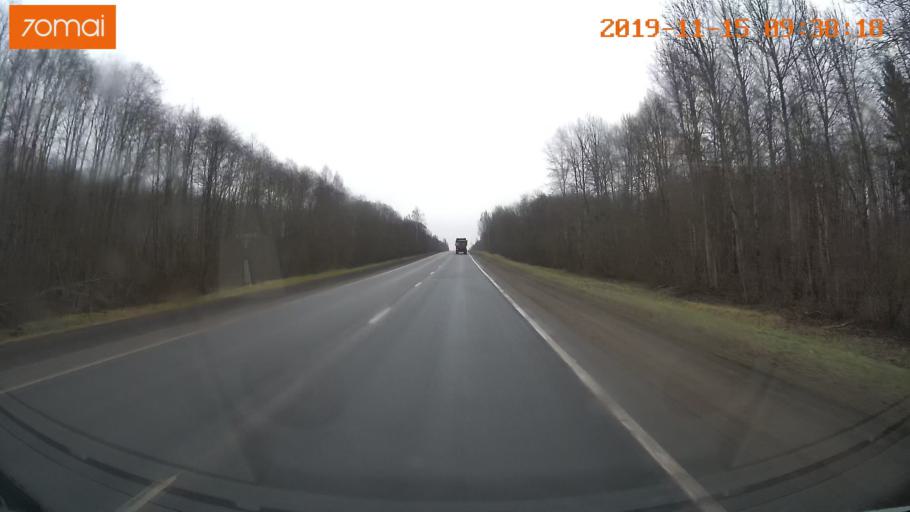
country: RU
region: Vologda
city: Sheksna
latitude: 59.2332
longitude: 38.4529
